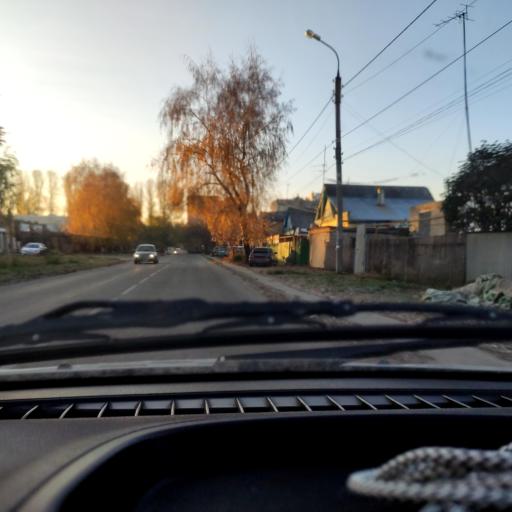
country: RU
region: Samara
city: Tol'yatti
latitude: 53.5345
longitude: 49.4289
